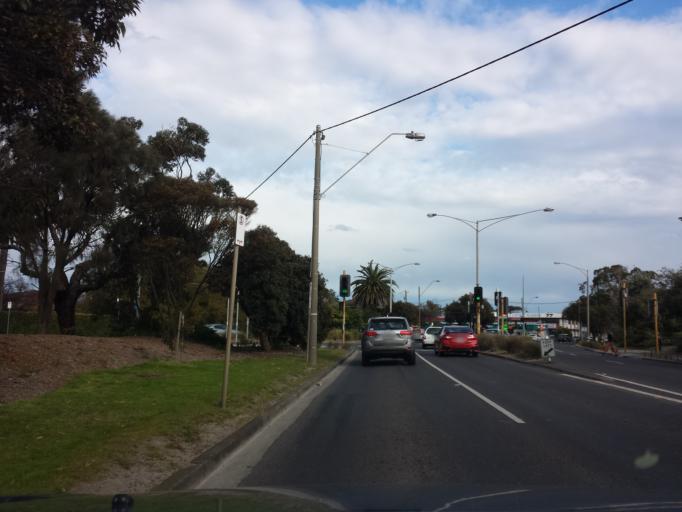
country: AU
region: Victoria
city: Hampton
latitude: -37.9432
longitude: 145.0010
